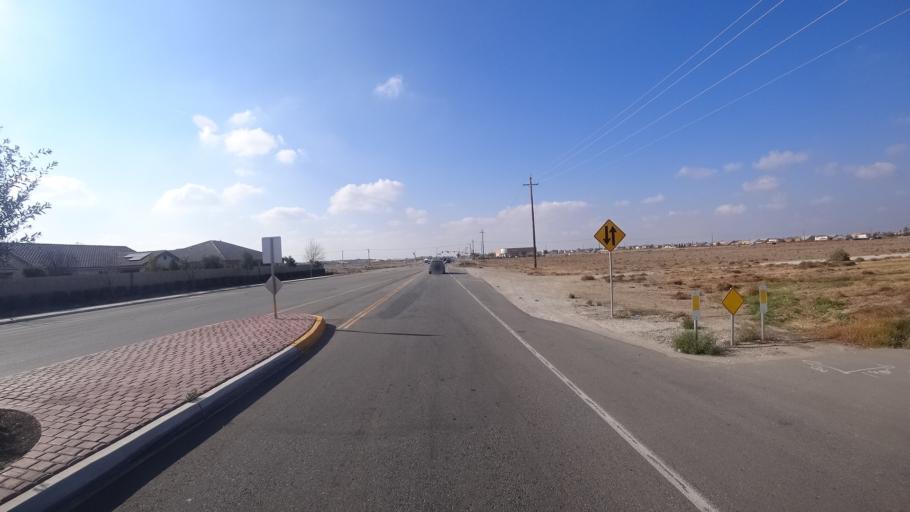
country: US
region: California
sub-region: Kern County
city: Greenacres
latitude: 35.2962
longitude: -119.1068
